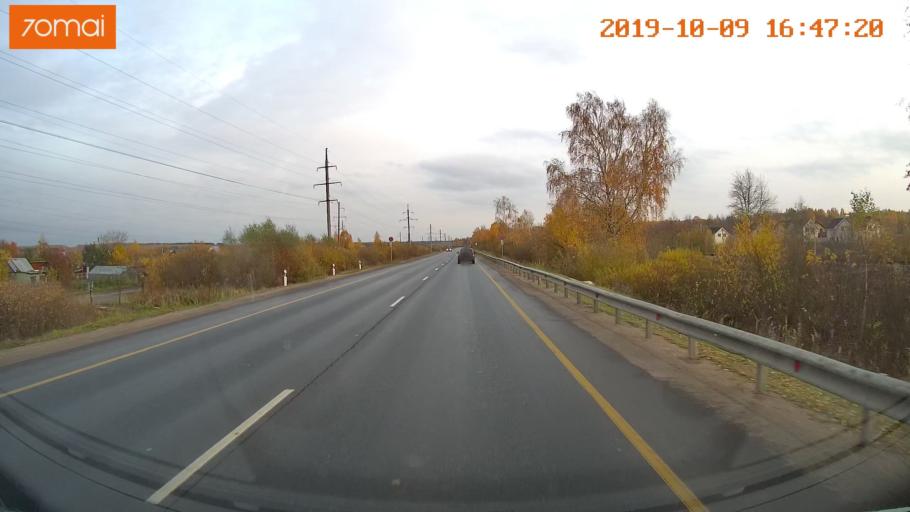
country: RU
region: Kostroma
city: Volgorechensk
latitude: 57.4374
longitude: 41.1767
